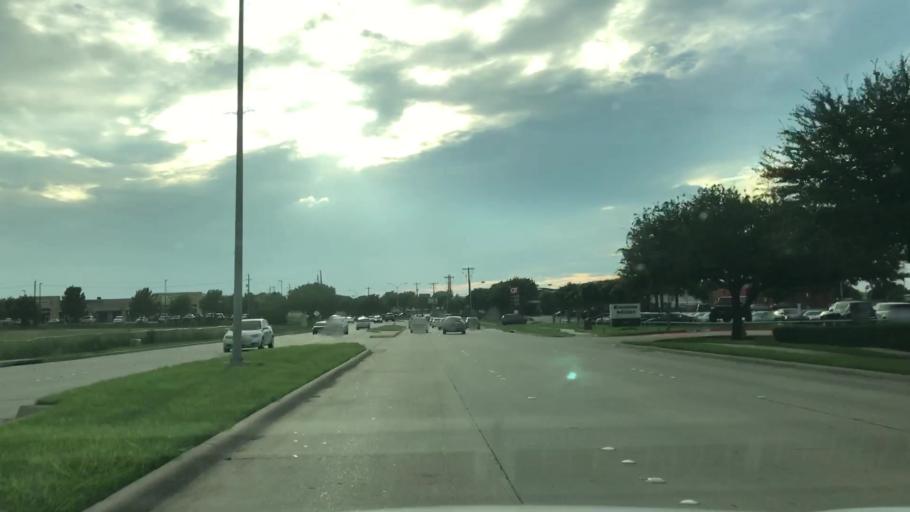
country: US
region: Texas
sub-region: Dallas County
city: Addison
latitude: 33.0276
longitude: -96.8371
